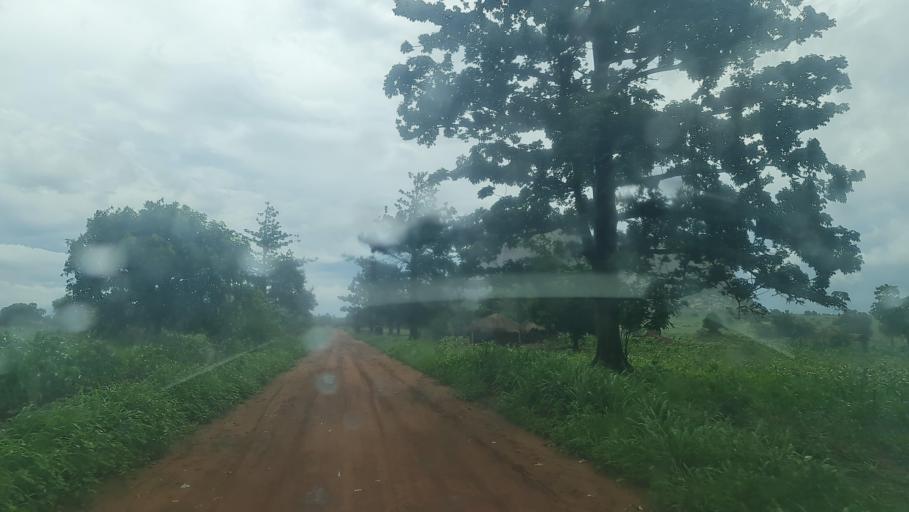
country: MW
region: Southern Region
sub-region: Nsanje District
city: Nsanje
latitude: -17.3996
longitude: 35.5889
